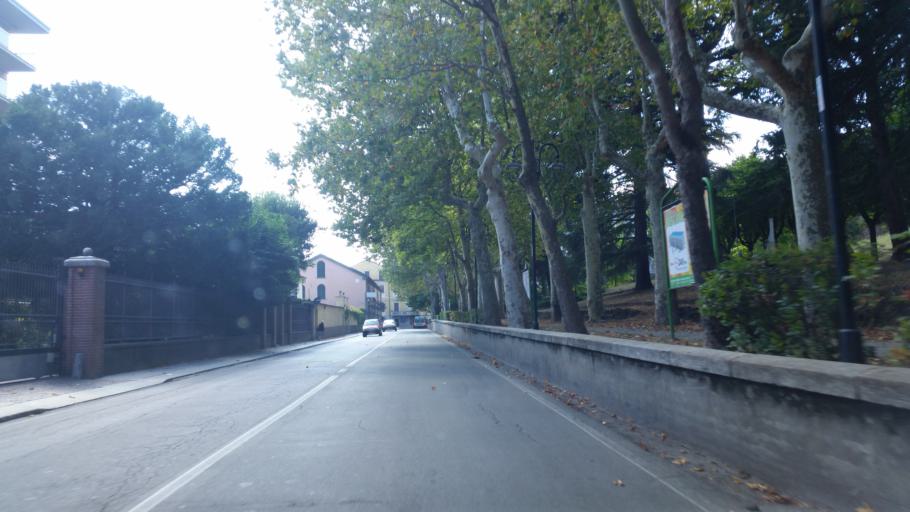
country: IT
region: Piedmont
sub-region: Provincia di Alessandria
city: Acqui Terme
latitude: 44.6730
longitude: 8.4729
